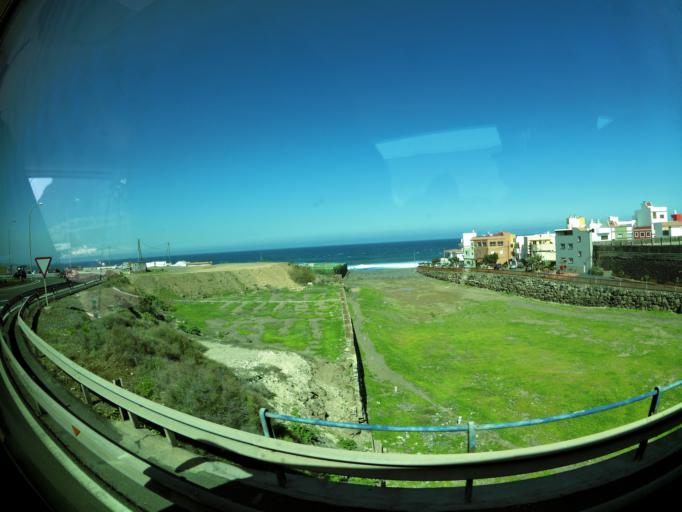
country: ES
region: Canary Islands
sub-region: Provincia de Las Palmas
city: Firgas
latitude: 28.1453
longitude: -15.5591
